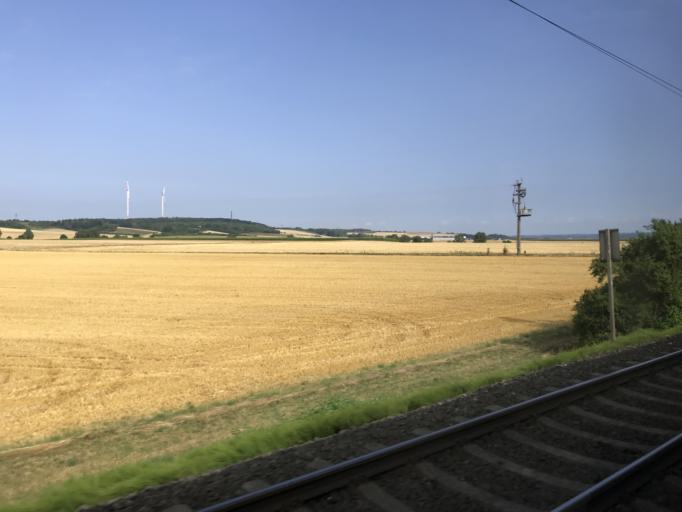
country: DE
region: Hesse
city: Bad Camberg
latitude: 50.2773
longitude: 8.2639
